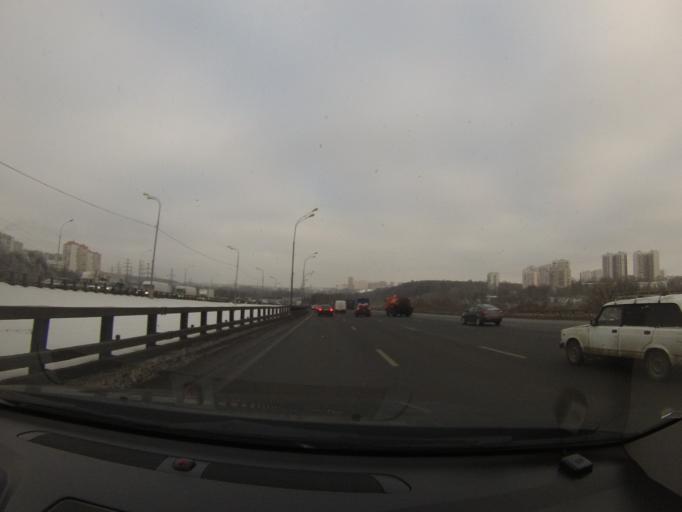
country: RU
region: Moscow
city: Strogino
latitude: 55.8393
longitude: 37.3952
